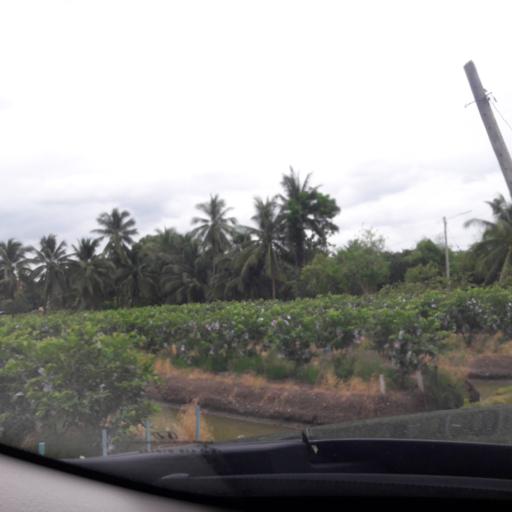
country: TH
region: Ratchaburi
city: Damnoen Saduak
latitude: 13.5702
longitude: 99.9509
